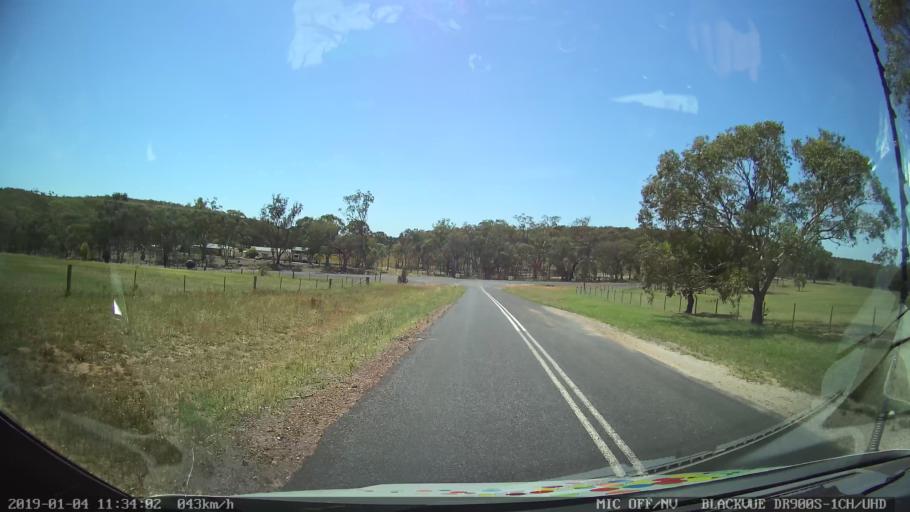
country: AU
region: New South Wales
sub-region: Cabonne
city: Molong
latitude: -33.0666
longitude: 148.8238
